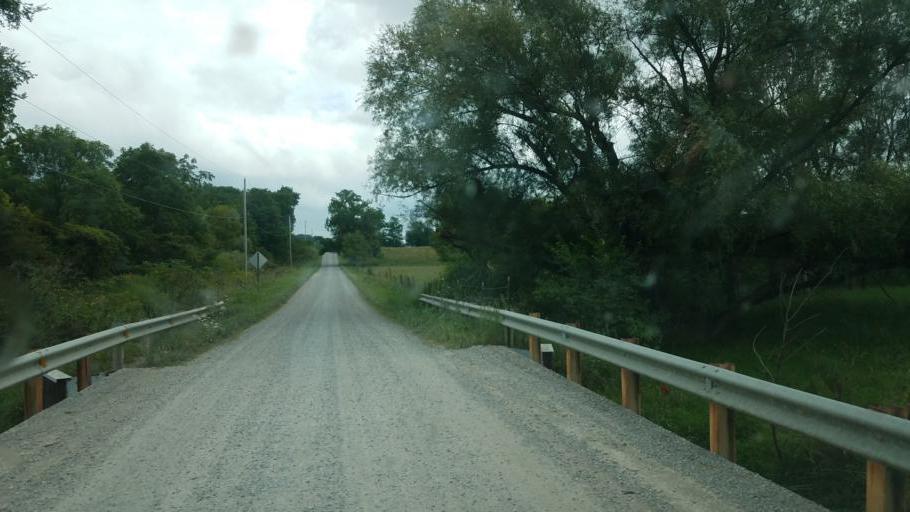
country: US
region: Ohio
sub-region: Morrow County
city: Mount Gilead
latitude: 40.5014
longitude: -82.7454
